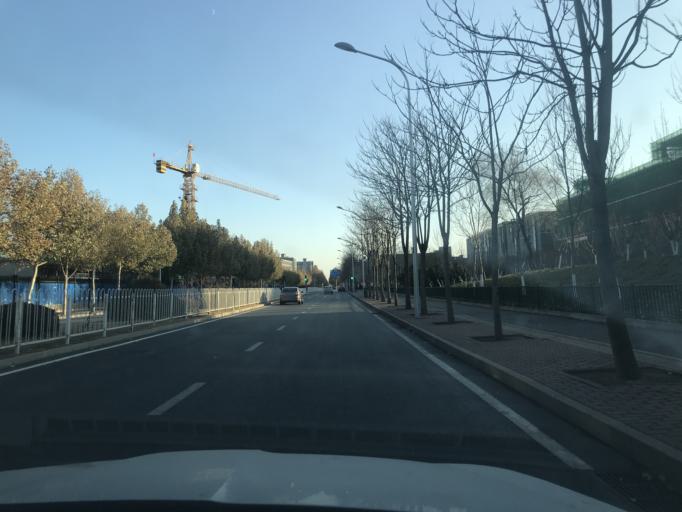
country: CN
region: Beijing
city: Xibeiwang
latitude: 40.0708
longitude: 116.2461
